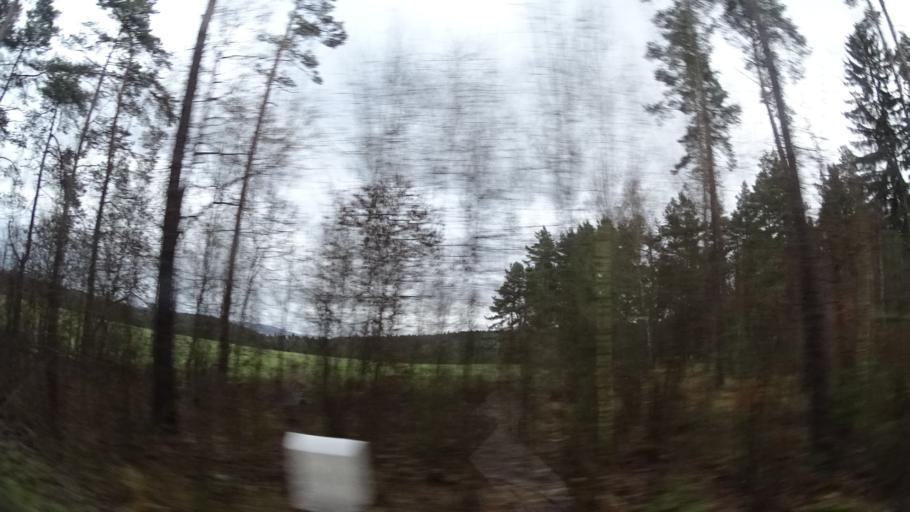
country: DE
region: Thuringia
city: Ellingshausen
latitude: 50.5741
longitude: 10.4616
